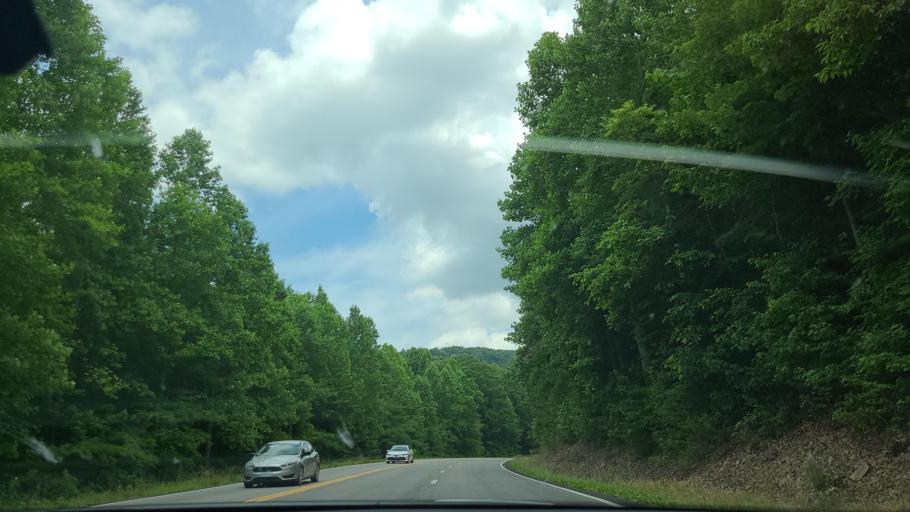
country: US
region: Tennessee
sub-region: Cumberland County
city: Lake Tansi
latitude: 35.7521
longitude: -85.0578
